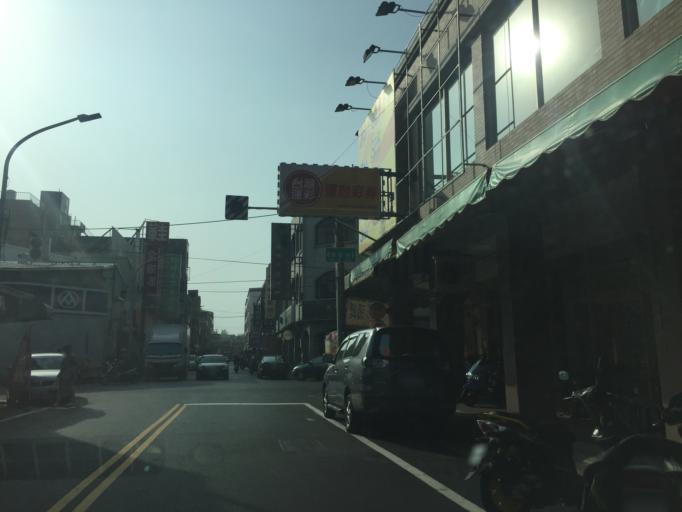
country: TW
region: Taiwan
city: Xinying
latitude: 23.1852
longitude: 120.2512
